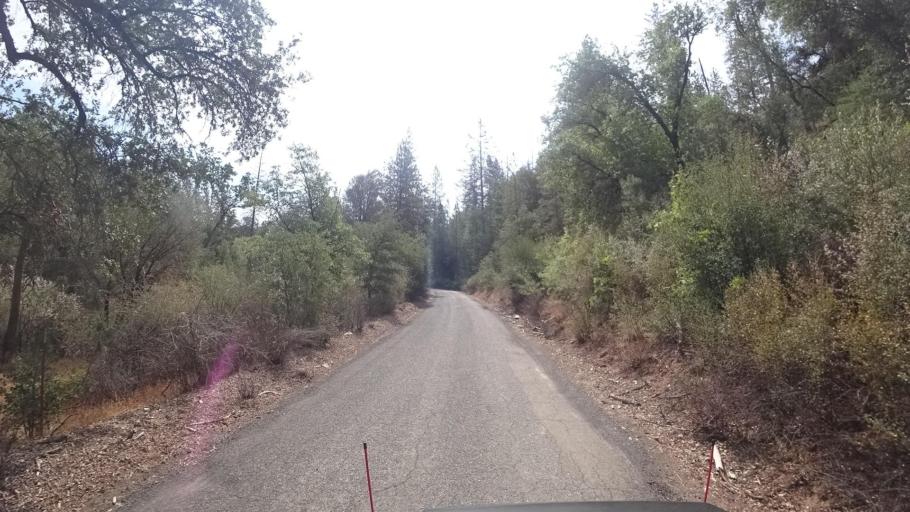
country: US
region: California
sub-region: Mariposa County
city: Midpines
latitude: 37.5654
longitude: -119.9842
